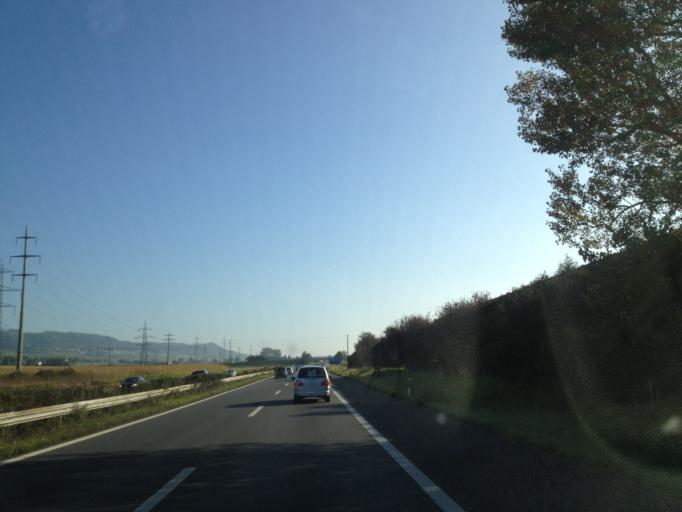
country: CH
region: Vaud
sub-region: Nyon District
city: Gland
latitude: 46.4404
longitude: 6.2847
